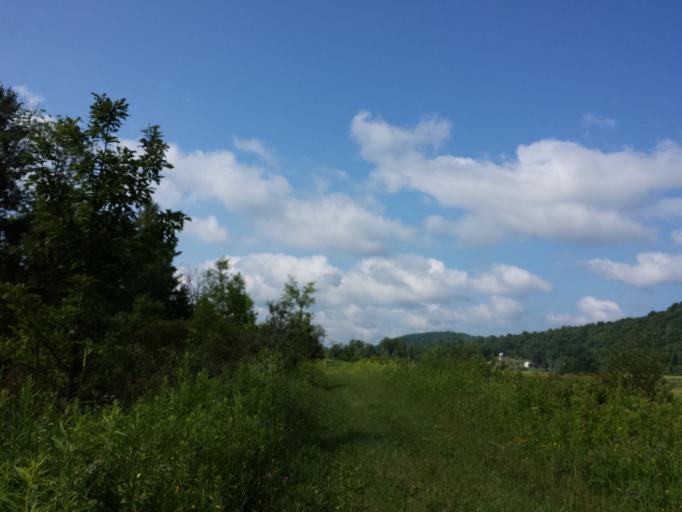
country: US
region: Vermont
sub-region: Rutland County
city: Poultney
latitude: 43.4903
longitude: -73.2495
